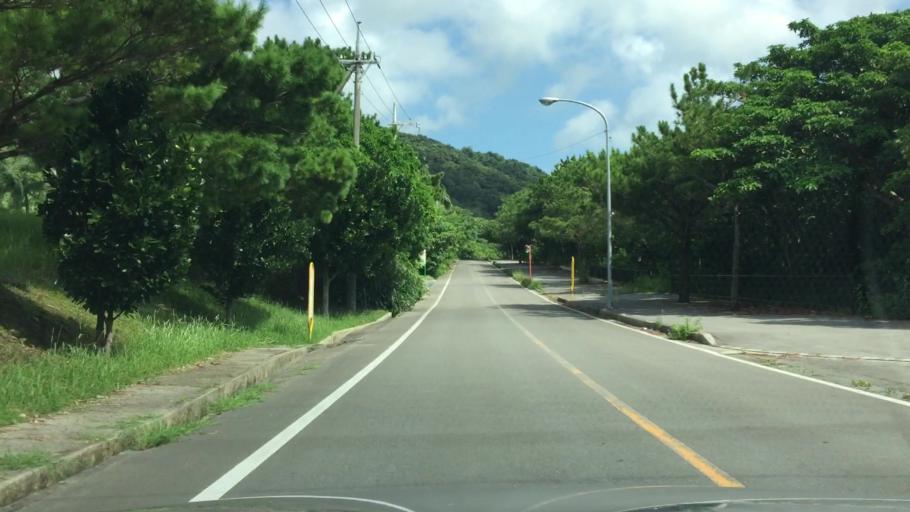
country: JP
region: Okinawa
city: Ishigaki
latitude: 24.4251
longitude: 124.2121
